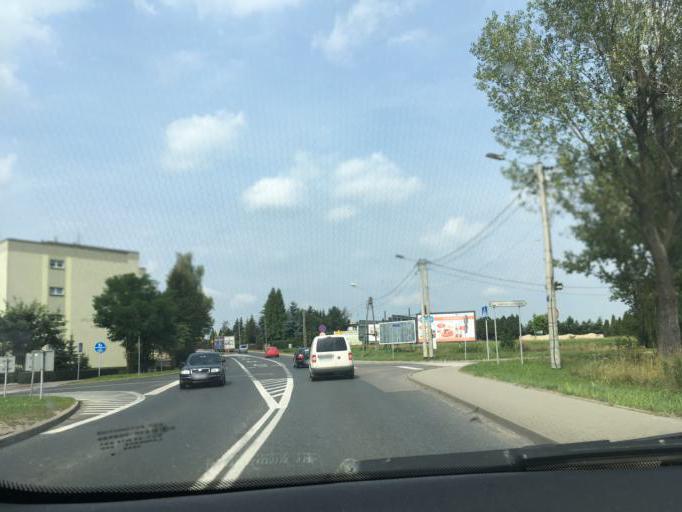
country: PL
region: Lesser Poland Voivodeship
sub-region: Powiat oswiecimski
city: Babice
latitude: 50.0771
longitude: 19.1764
